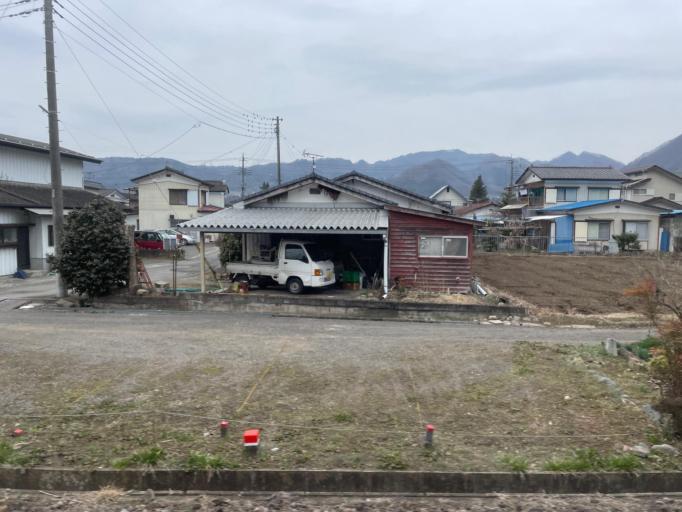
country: JP
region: Gunma
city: Numata
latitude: 36.6594
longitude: 139.0257
